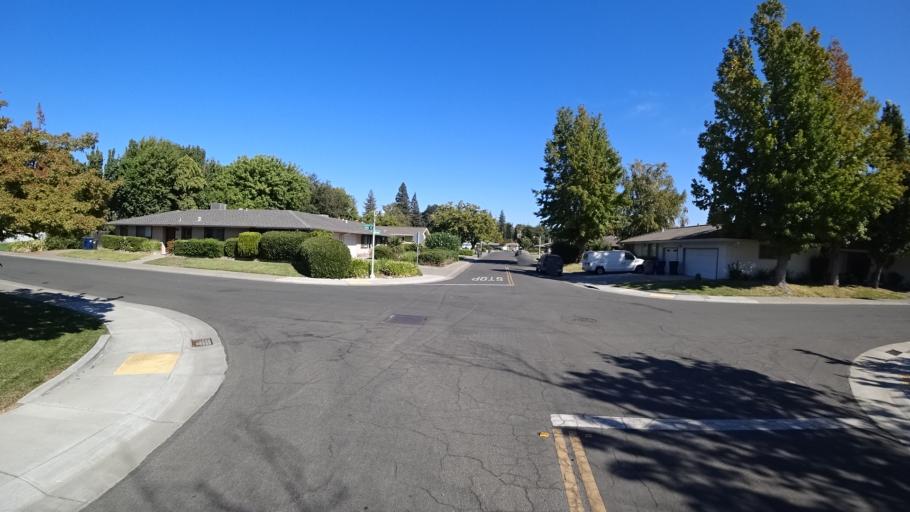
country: US
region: California
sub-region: Sacramento County
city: Parkway
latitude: 38.5016
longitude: -121.5215
